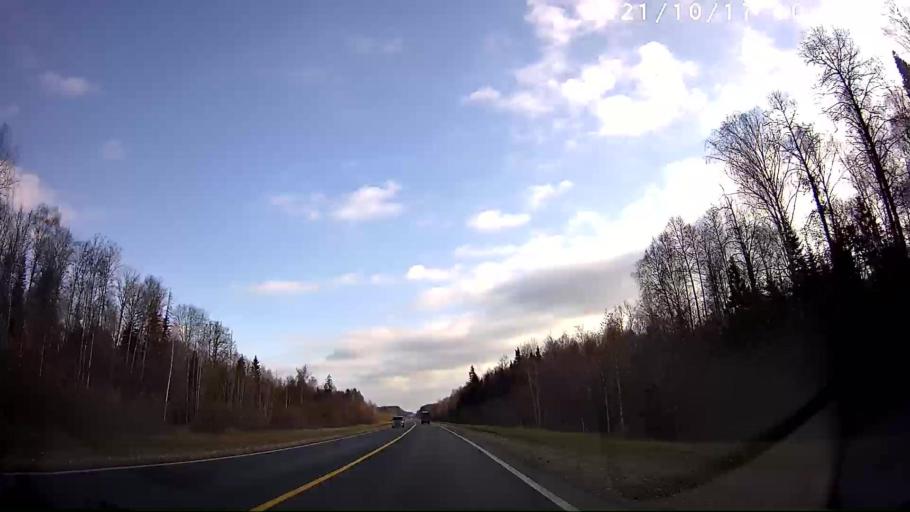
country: RU
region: Mariy-El
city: Sovetskiy
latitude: 56.7392
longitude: 48.4094
